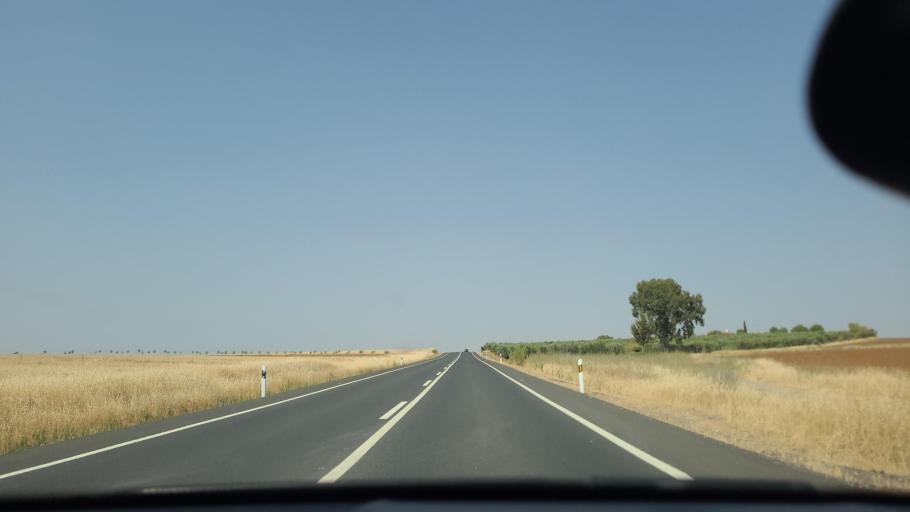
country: ES
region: Extremadura
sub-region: Provincia de Badajoz
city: Ahillones
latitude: 38.2588
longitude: -5.8781
